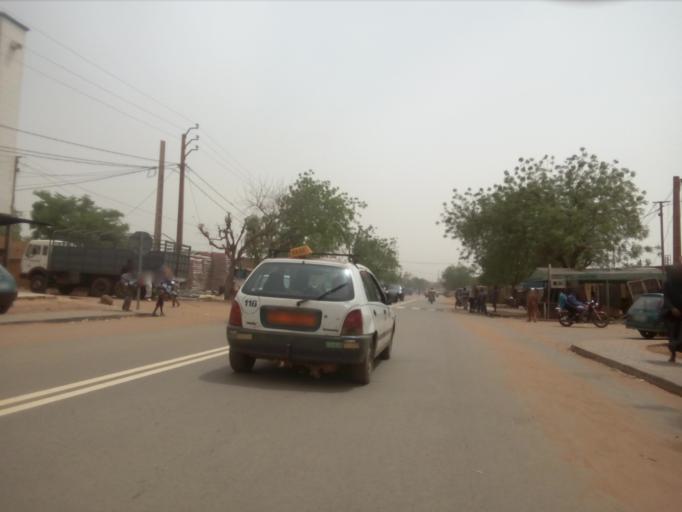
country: NE
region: Niamey
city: Niamey
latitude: 13.5292
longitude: 2.1222
